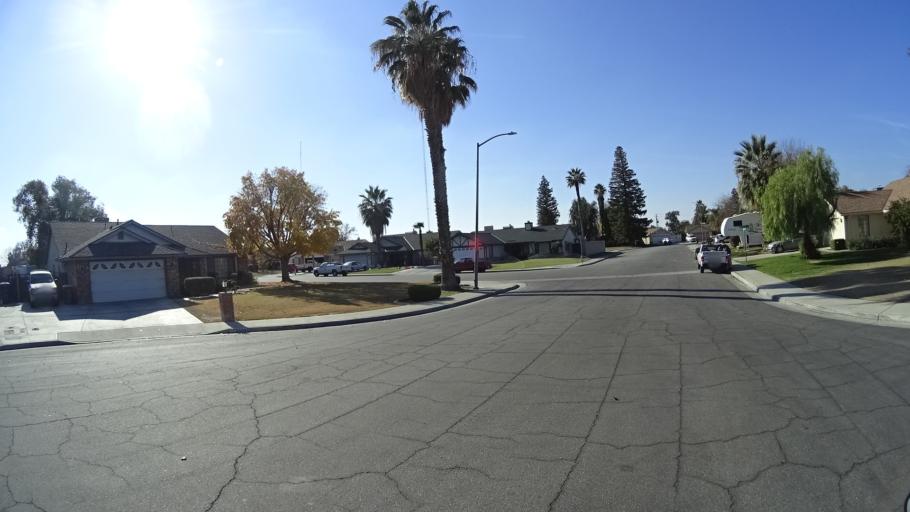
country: US
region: California
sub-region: Kern County
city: Greenfield
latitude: 35.3089
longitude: -119.0416
